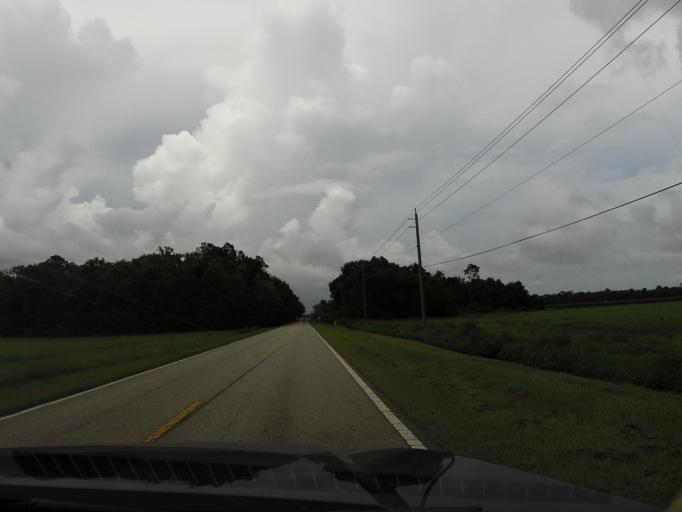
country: US
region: Florida
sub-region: Putnam County
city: East Palatka
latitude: 29.8481
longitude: -81.5297
